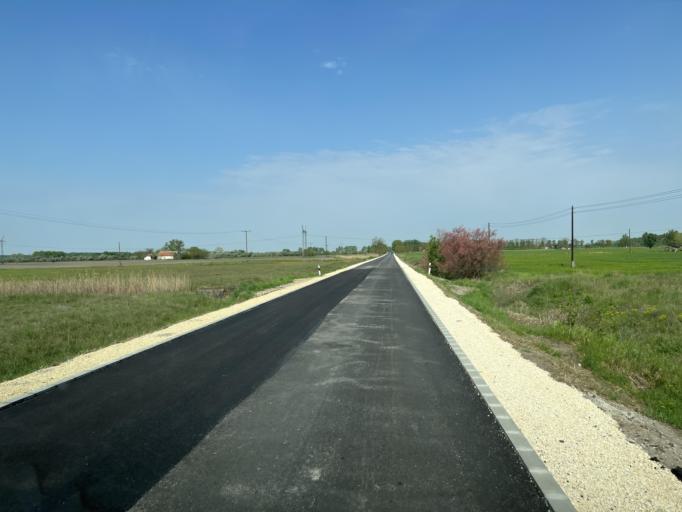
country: HU
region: Pest
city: Kocser
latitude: 46.9933
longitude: 19.9542
